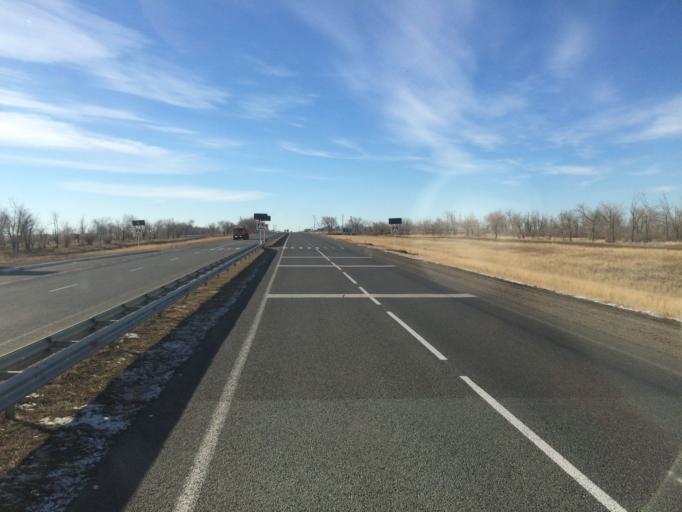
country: KZ
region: Aqtoebe
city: Aqtobe
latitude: 50.2654
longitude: 56.9595
